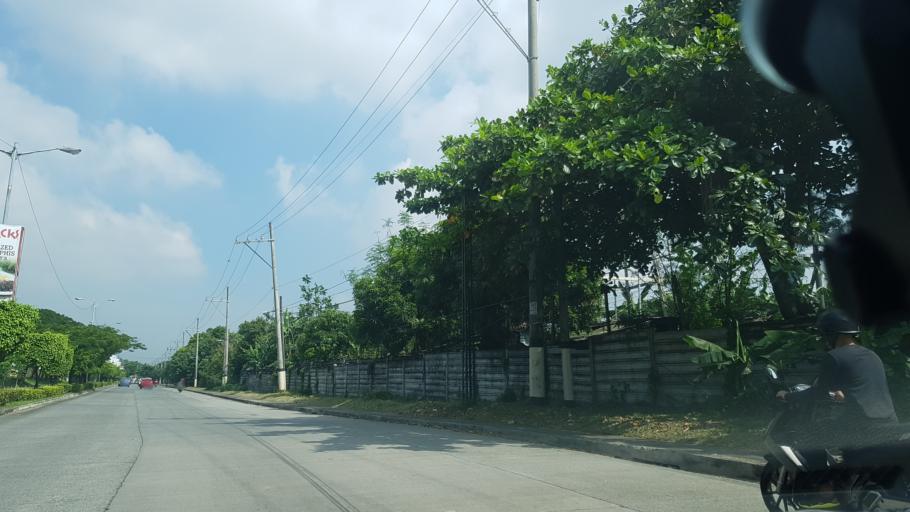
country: PH
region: Calabarzon
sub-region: Province of Laguna
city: San Pedro
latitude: 14.3804
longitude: 121.0134
